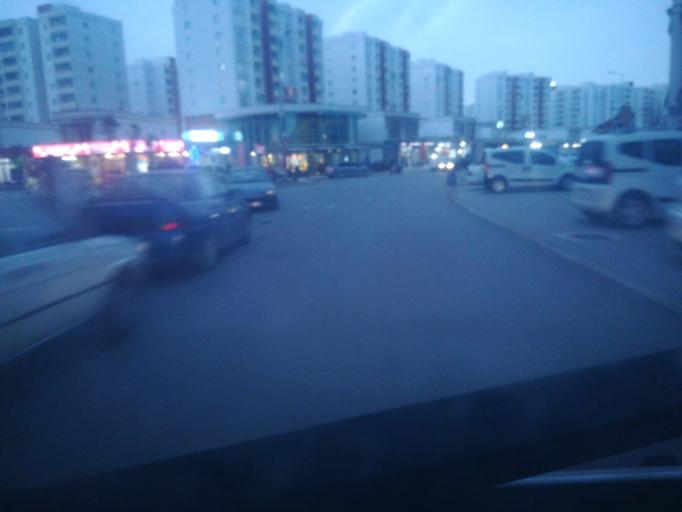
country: TR
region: Adana
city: Seyhan
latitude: 37.0089
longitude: 35.2784
